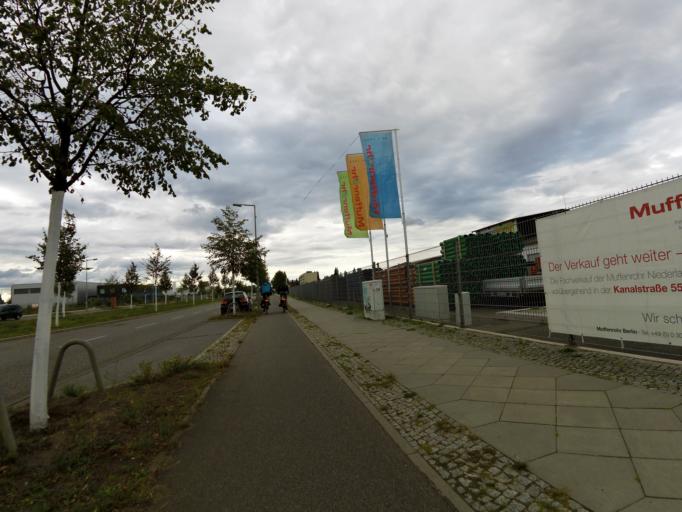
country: DE
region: Berlin
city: Niederschoneweide
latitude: 52.4403
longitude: 13.5236
